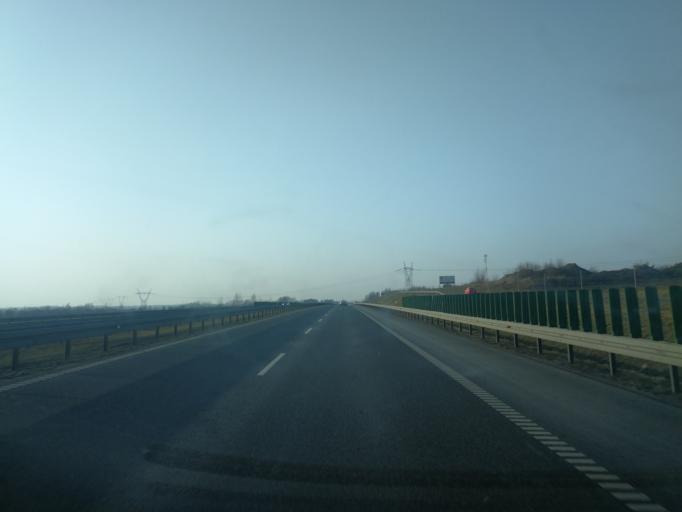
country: PL
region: Warmian-Masurian Voivodeship
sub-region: Powiat elblaski
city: Gronowo Gorne
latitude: 54.1169
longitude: 19.4769
